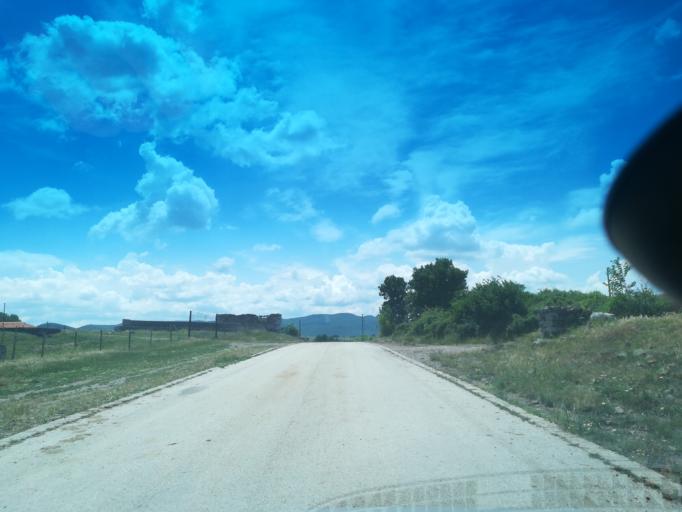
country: BG
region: Khaskovo
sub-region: Obshtina Mineralni Bani
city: Mineralni Bani
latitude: 41.9510
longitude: 25.2481
